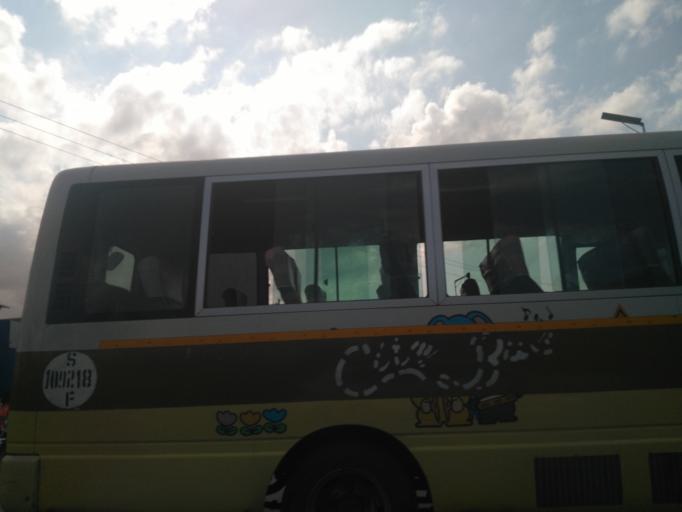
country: TZ
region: Dar es Salaam
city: Dar es Salaam
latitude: -6.8972
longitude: 39.2836
